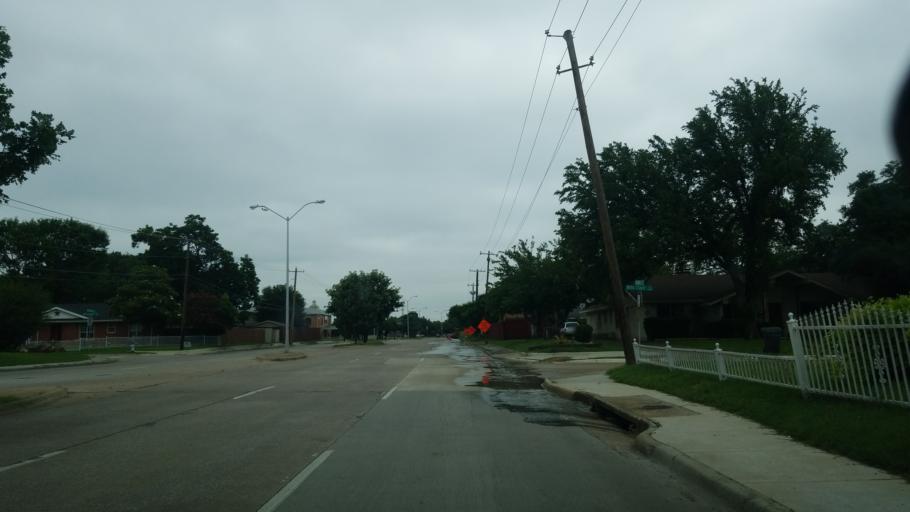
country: US
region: Texas
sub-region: Dallas County
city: Farmers Branch
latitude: 32.9016
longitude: -96.8722
